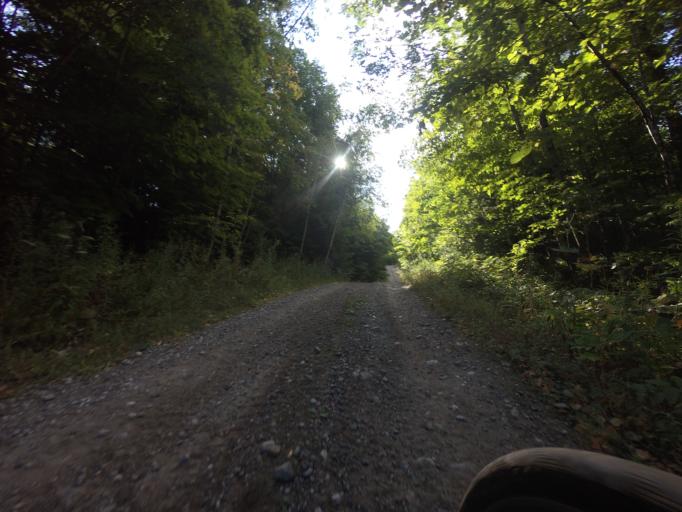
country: CA
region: Ontario
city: Arnprior
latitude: 45.1917
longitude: -76.5211
